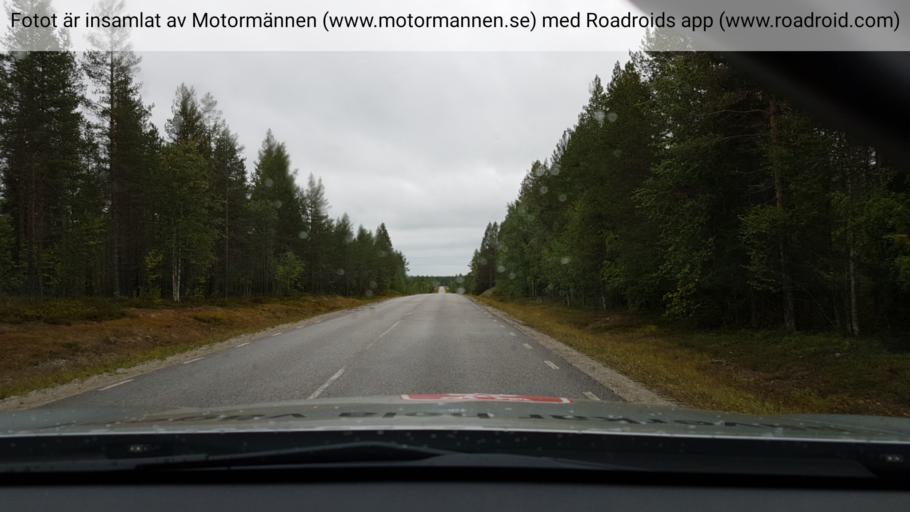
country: SE
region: Vaesterbotten
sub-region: Skelleftea Kommun
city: Langsele
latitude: 65.0890
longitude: 20.0820
